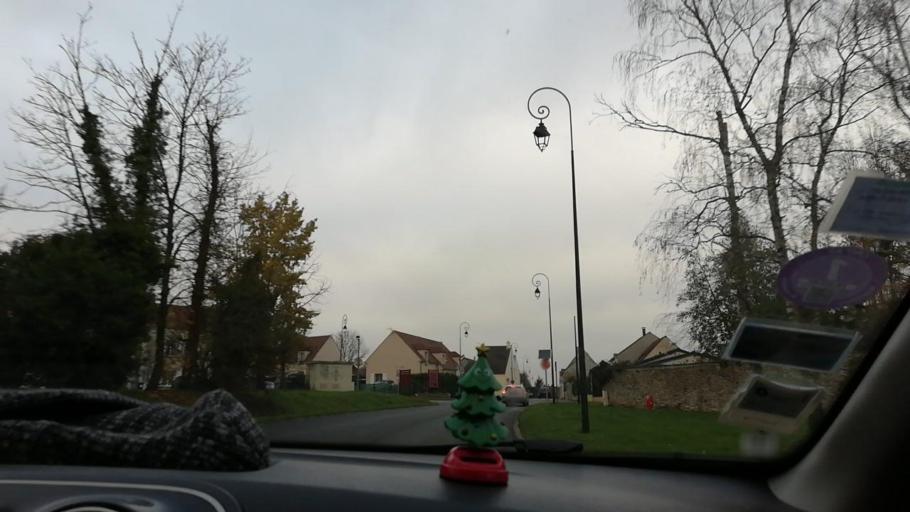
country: FR
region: Ile-de-France
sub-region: Departement de Seine-et-Marne
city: Monthyon
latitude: 49.0031
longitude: 2.8291
